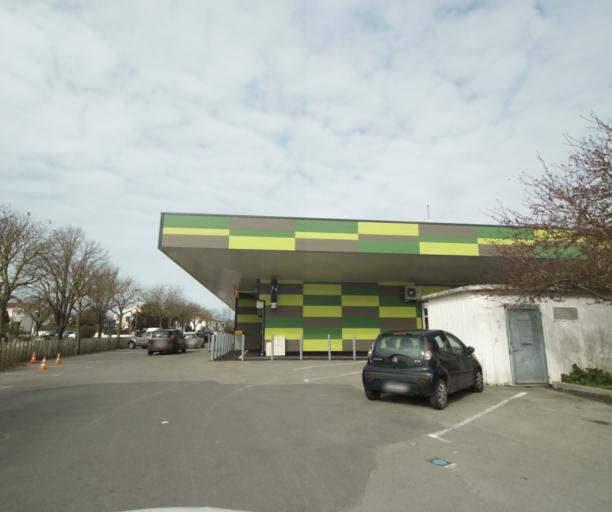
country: FR
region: Poitou-Charentes
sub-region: Departement de la Charente-Maritime
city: Lagord
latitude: 46.1838
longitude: -1.1555
